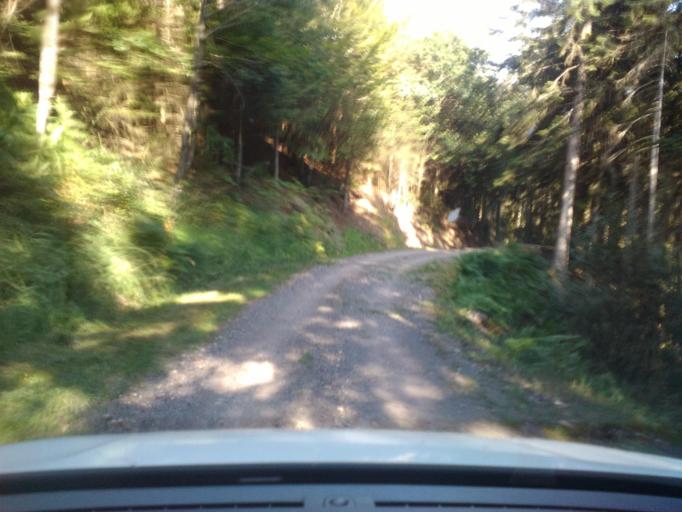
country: FR
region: Lorraine
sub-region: Departement des Vosges
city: Senones
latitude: 48.4179
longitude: 6.9811
